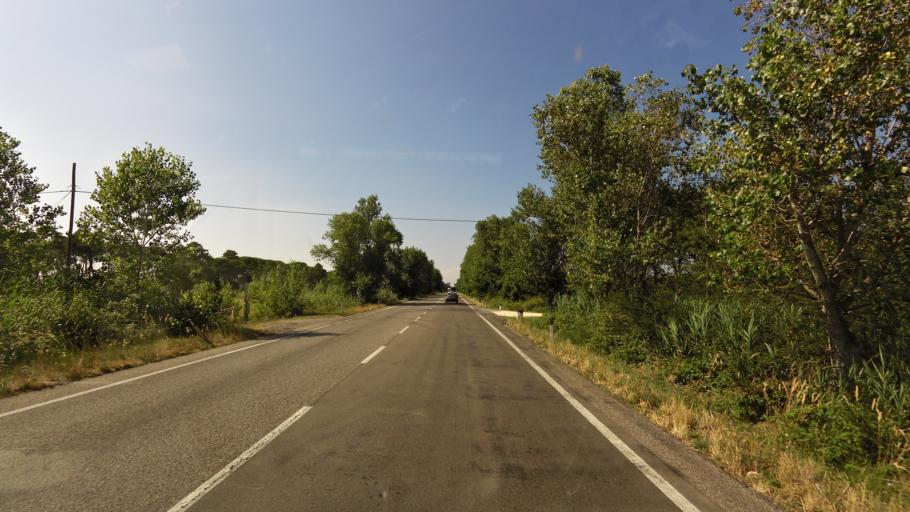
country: IT
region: Emilia-Romagna
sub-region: Provincia di Ferrara
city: Lido degli Estensi
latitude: 44.5904
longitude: 12.2510
